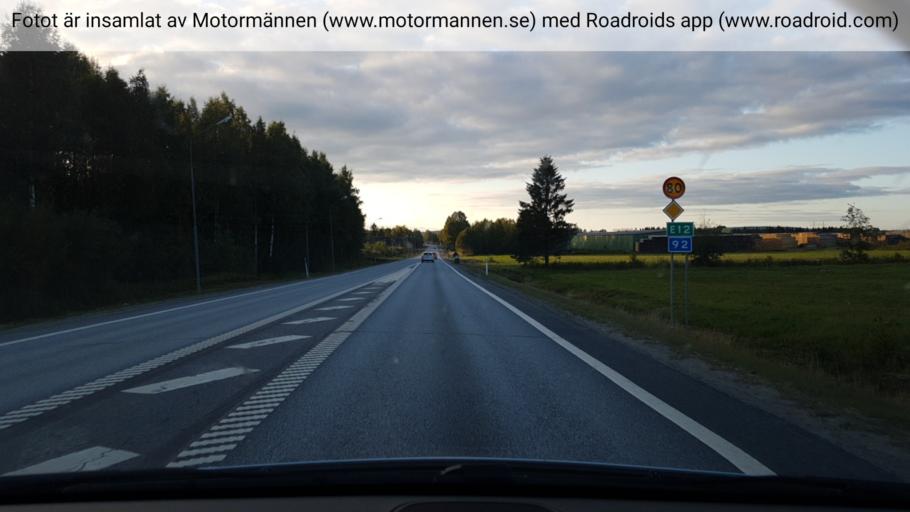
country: SE
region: Vaesterbotten
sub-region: Vannas Kommun
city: Vannasby
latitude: 63.9139
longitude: 19.8823
